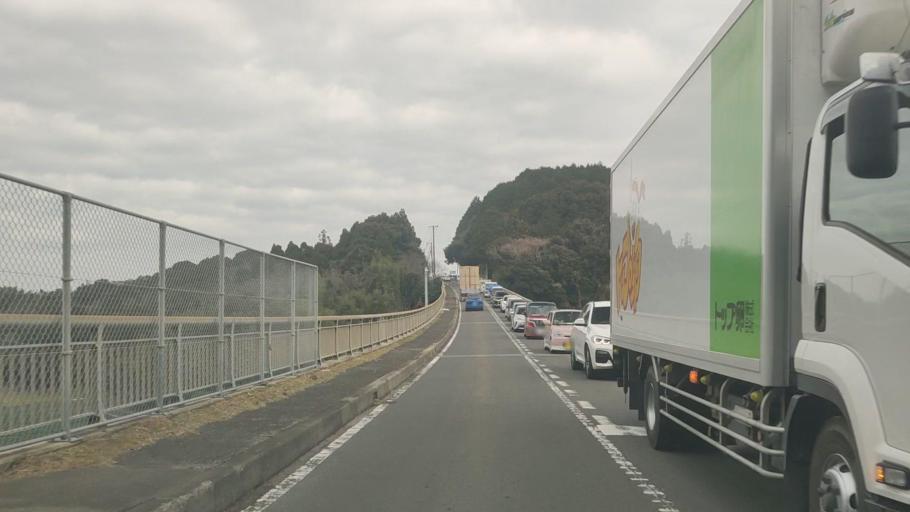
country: JP
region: Nagasaki
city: Shimabara
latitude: 32.8368
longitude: 130.2135
